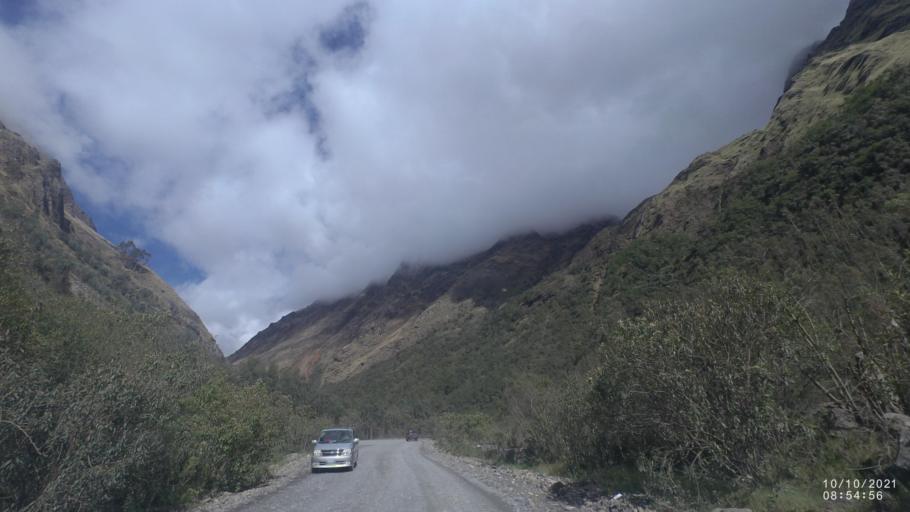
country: BO
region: La Paz
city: Quime
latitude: -16.9873
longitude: -67.2384
